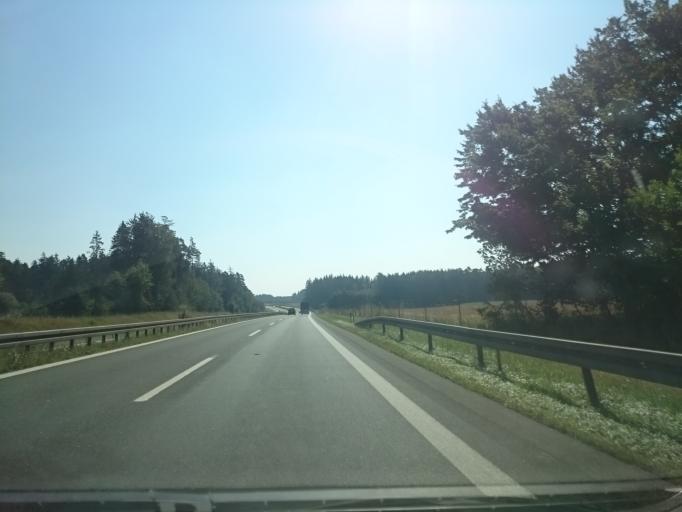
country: DE
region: Bavaria
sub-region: Upper Franconia
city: Stadelhofen
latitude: 50.0088
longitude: 11.2471
